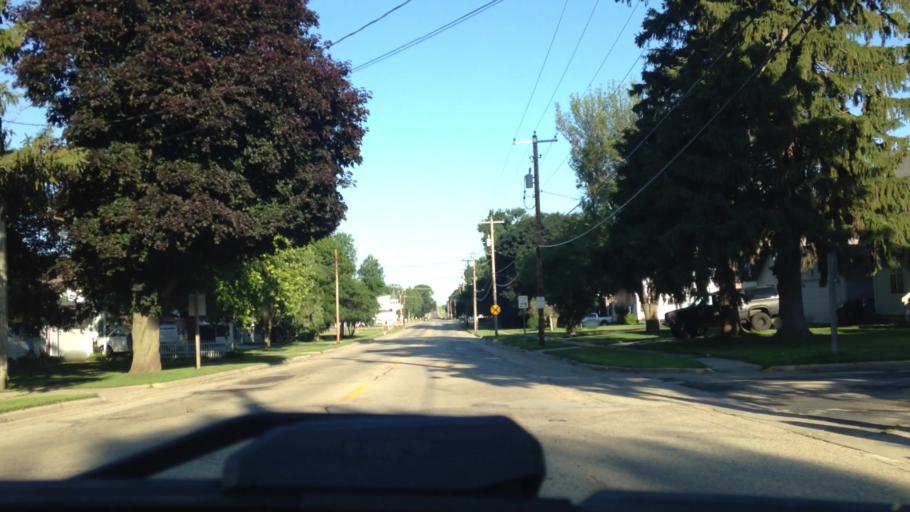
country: US
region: Wisconsin
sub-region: Columbia County
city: Poynette
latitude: 43.3376
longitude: -89.3751
